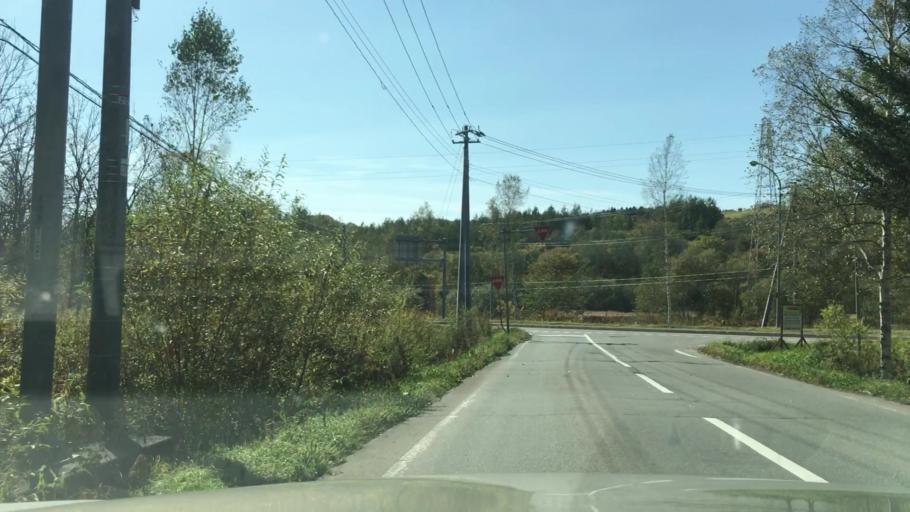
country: JP
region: Hokkaido
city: Kitami
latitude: 43.5844
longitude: 143.6818
